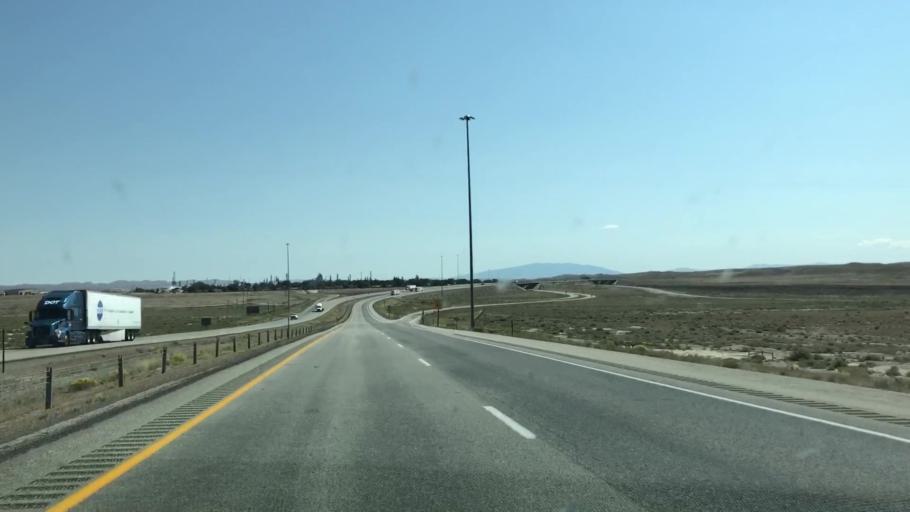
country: US
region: Wyoming
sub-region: Carbon County
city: Rawlins
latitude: 41.7812
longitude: -107.1390
